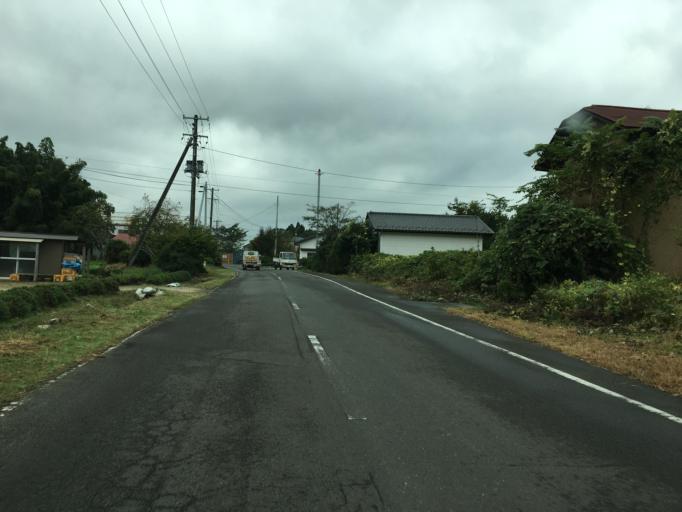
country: JP
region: Fukushima
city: Nihommatsu
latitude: 37.6209
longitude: 140.4413
